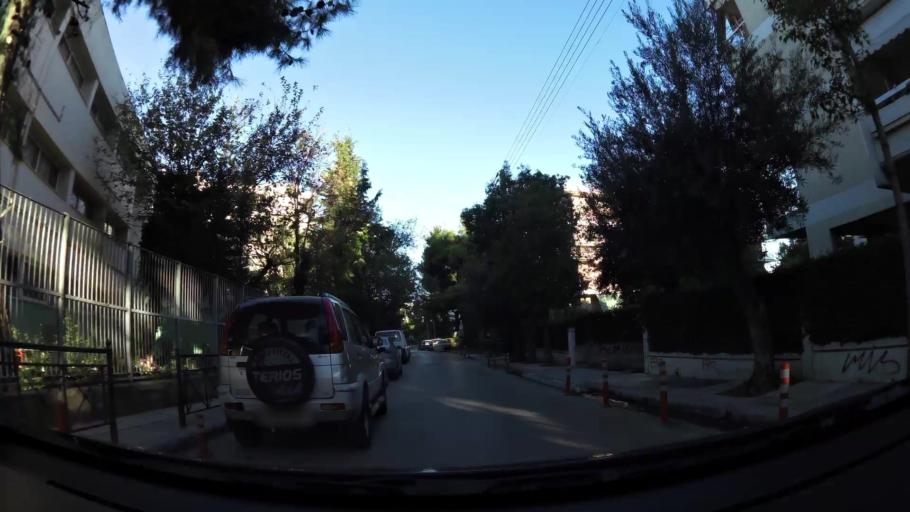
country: GR
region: Attica
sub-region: Nomarchia Athinas
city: Cholargos
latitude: 38.0100
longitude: 23.7980
